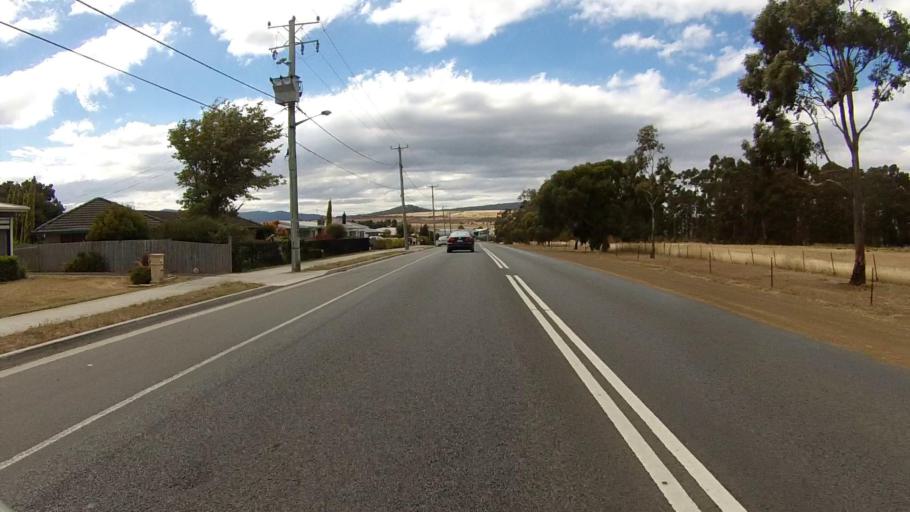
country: AU
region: Tasmania
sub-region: Sorell
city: Sorell
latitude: -42.7917
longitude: 147.5579
